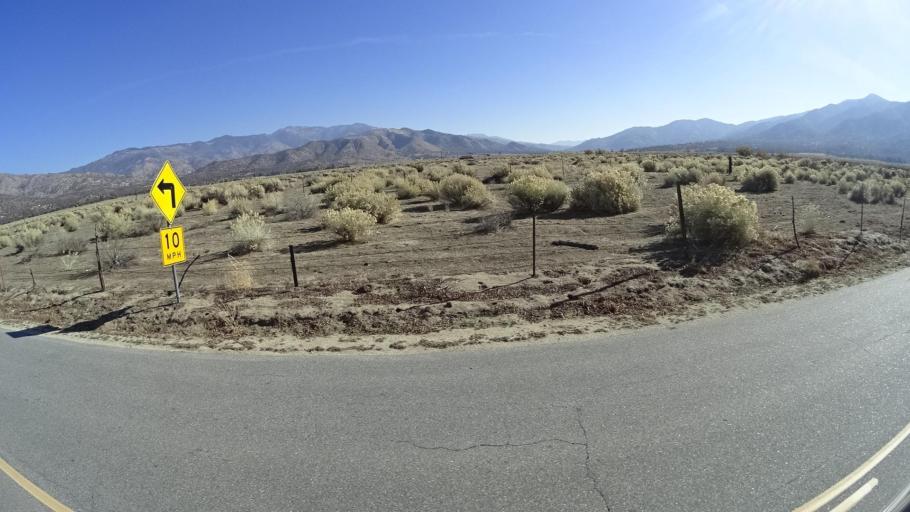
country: US
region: California
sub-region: Kern County
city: Bodfish
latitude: 35.4085
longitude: -118.5256
